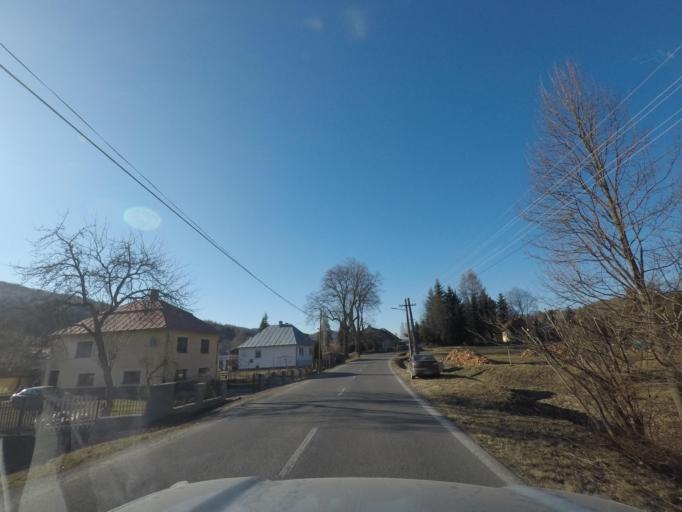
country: SK
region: Presovsky
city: Medzilaborce
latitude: 49.1902
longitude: 22.0071
